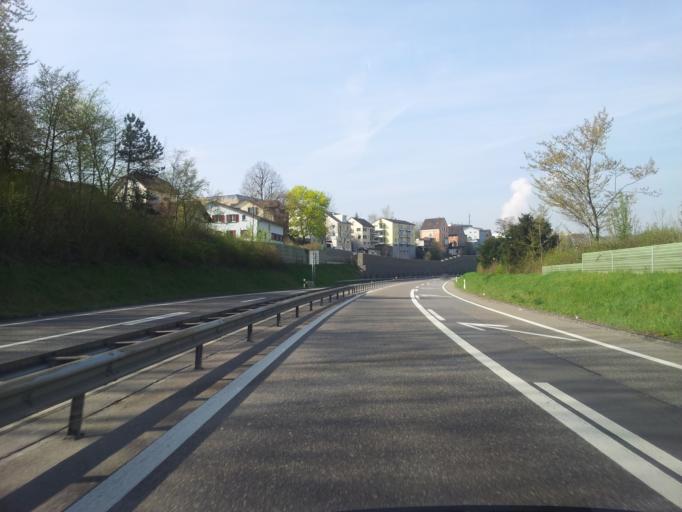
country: CH
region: Aargau
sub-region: Bezirk Aarau
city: Buchs
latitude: 47.3970
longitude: 8.0669
